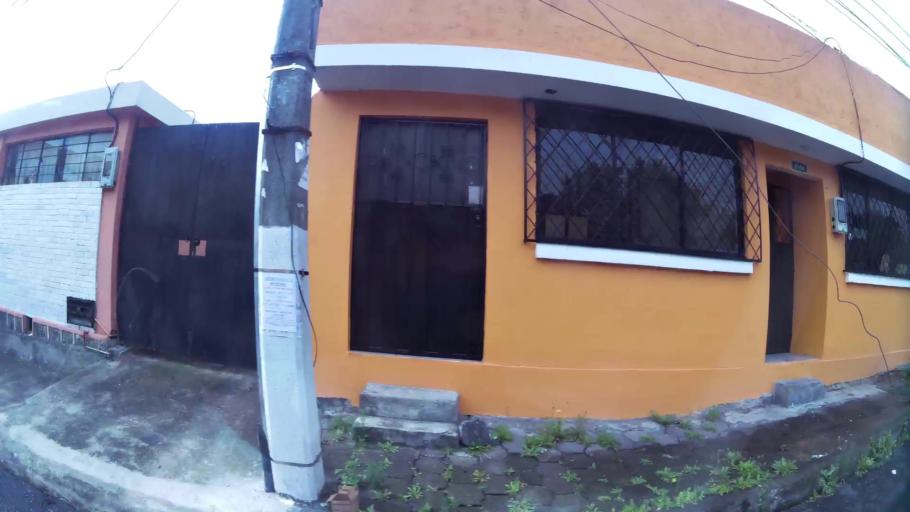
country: EC
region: Pichincha
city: Sangolqui
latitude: -0.2939
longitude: -78.4749
